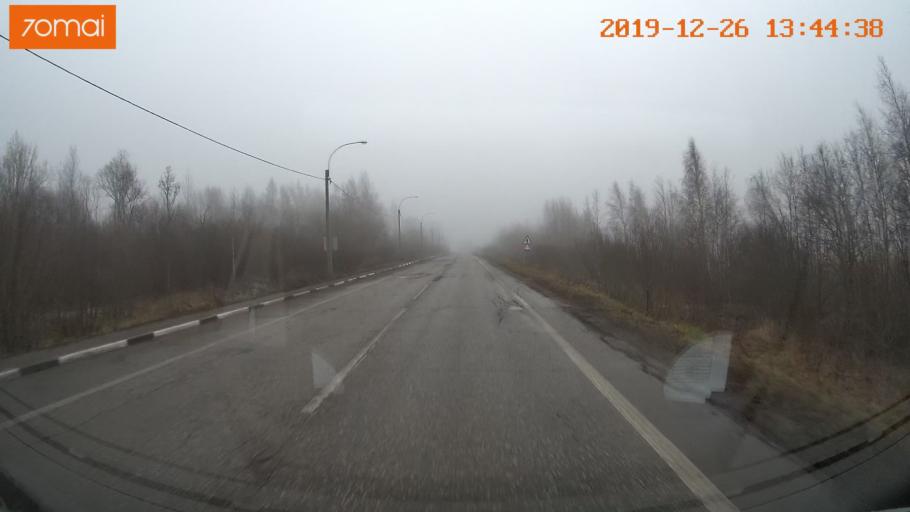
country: RU
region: Vologda
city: Sheksna
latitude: 58.7005
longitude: 38.5090
